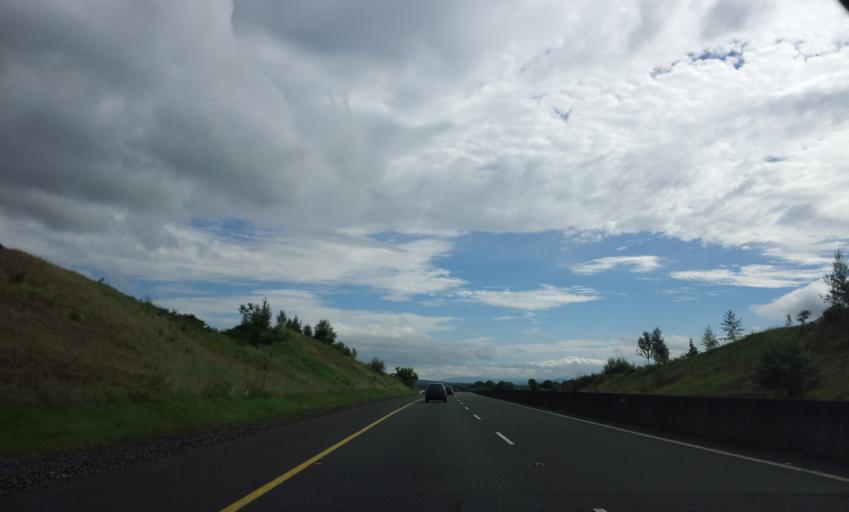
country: IE
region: Munster
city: Ballina
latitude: 52.7914
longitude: -8.3465
